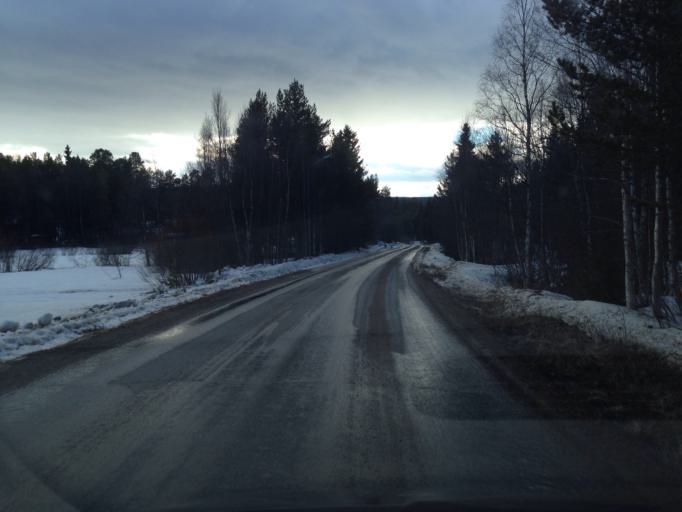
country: SE
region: Jaemtland
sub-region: Harjedalens Kommun
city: Sveg
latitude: 62.1165
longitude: 13.2685
